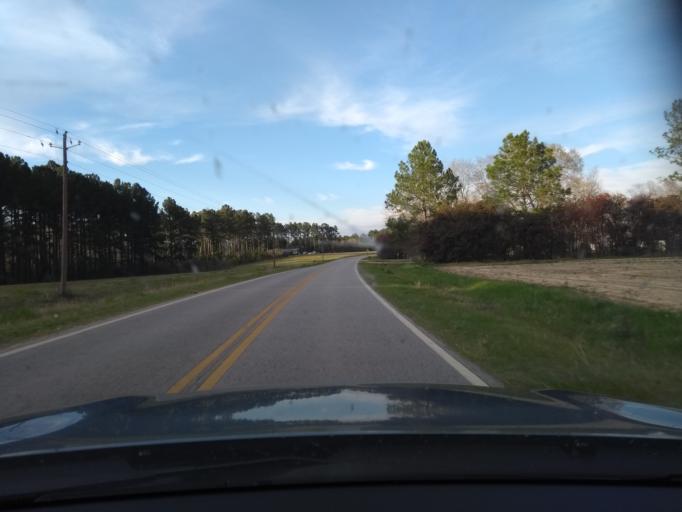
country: US
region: Georgia
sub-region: Bulloch County
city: Brooklet
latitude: 32.3179
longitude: -81.7784
